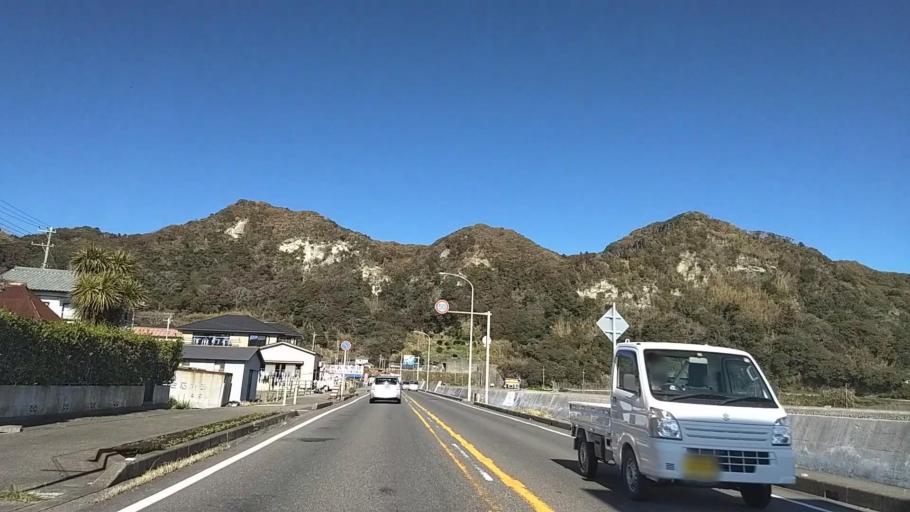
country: JP
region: Chiba
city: Kawaguchi
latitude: 35.0709
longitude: 140.0844
